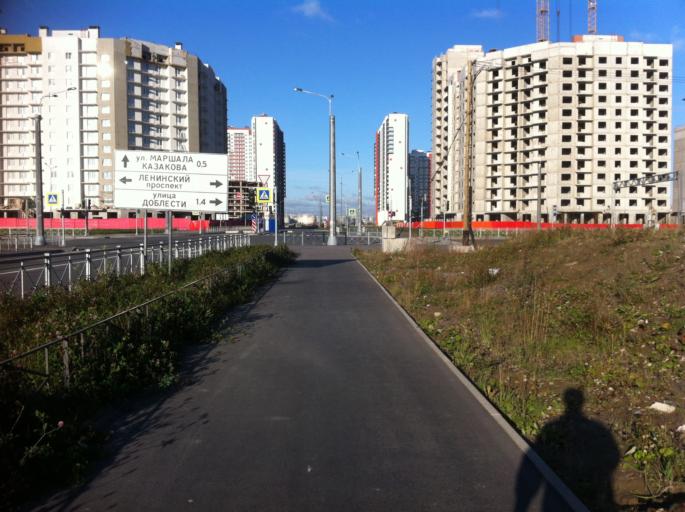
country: RU
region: St.-Petersburg
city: Sosnovaya Polyana
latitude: 59.8659
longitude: 30.1564
